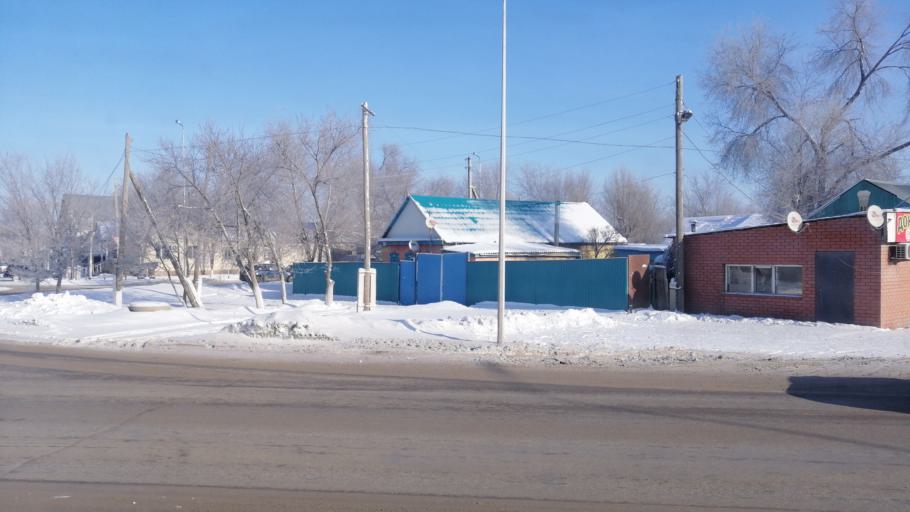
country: KZ
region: Aqtoebe
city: Aqtobe
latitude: 50.2909
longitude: 57.2021
